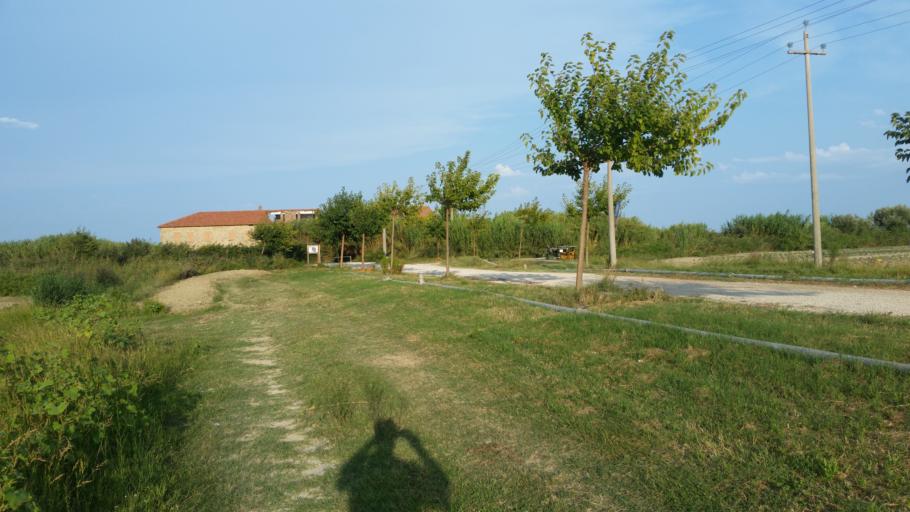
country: IT
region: Abruzzo
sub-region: Provincia di Teramo
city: Martinsicuro
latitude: 42.8992
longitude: 13.9080
